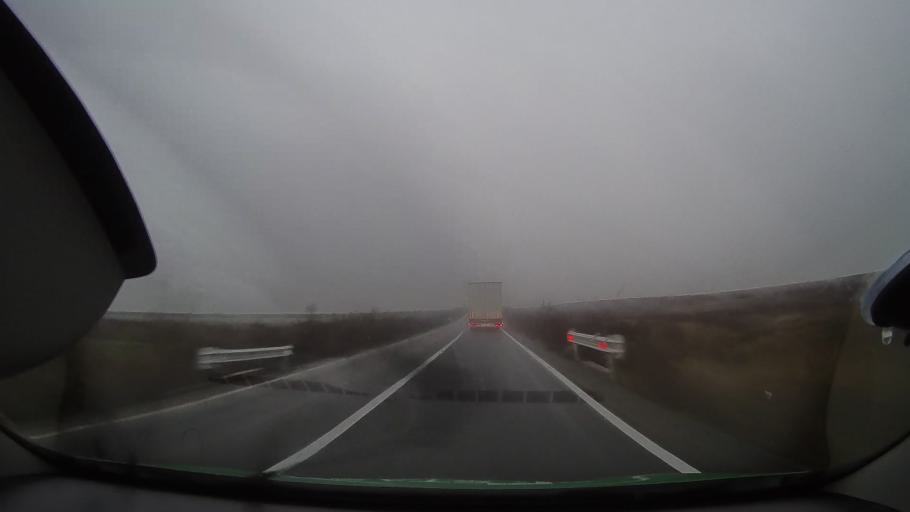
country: RO
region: Bihor
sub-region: Comuna Olcea
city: Olcea
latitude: 46.6687
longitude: 21.9639
